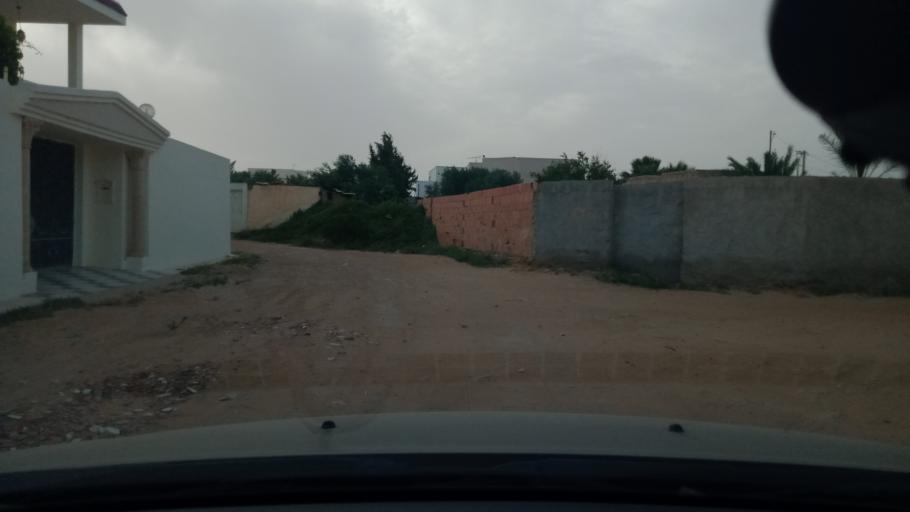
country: TN
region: Safaqis
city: Al Qarmadah
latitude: 34.7901
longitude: 10.7692
